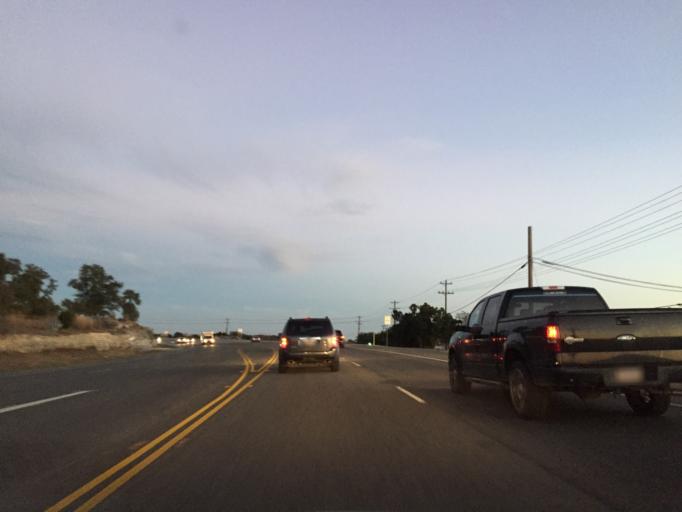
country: US
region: Texas
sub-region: Williamson County
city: Cedar Park
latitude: 30.5132
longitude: -97.8648
